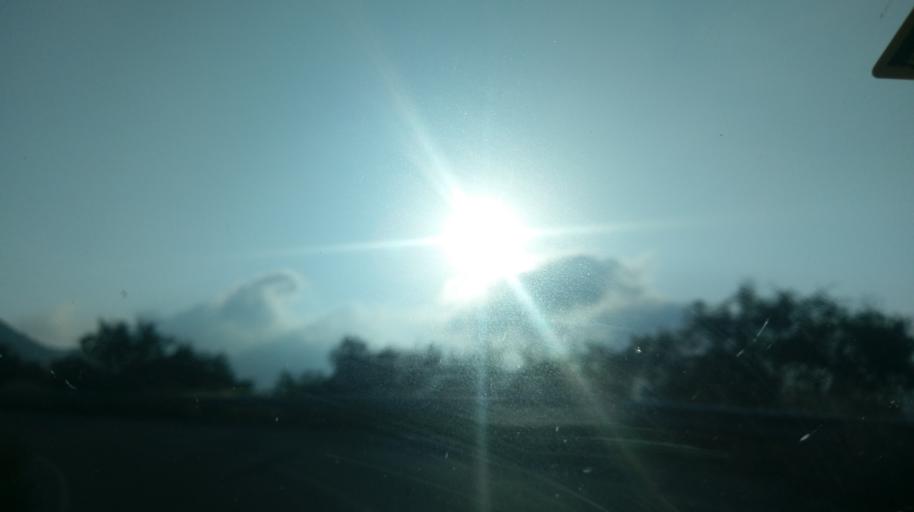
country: CY
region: Ammochostos
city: Trikomo
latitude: 35.4048
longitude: 33.9031
